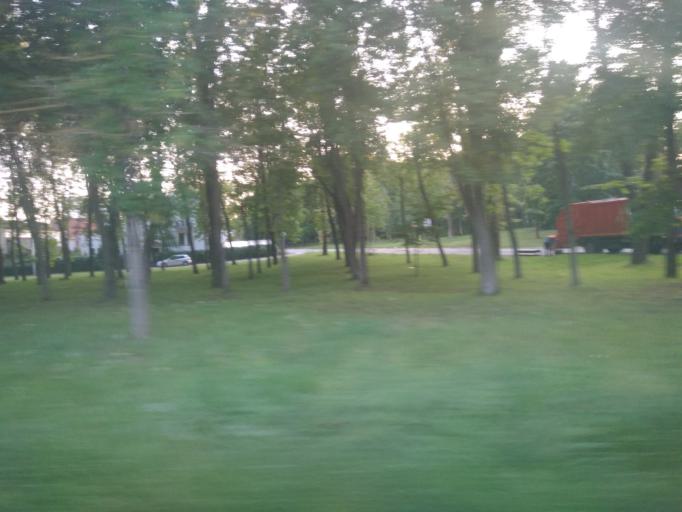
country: BY
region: Minsk
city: Minsk
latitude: 53.9394
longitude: 27.5505
